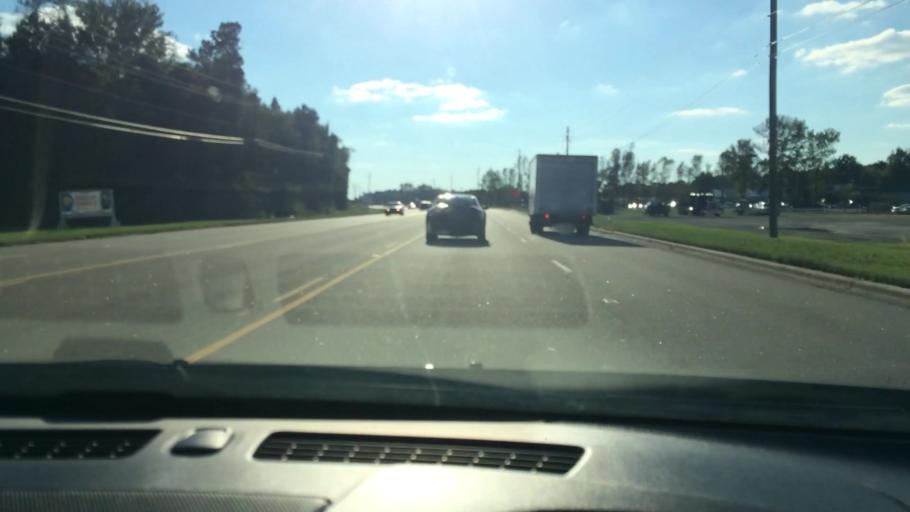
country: US
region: North Carolina
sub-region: Pitt County
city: Summerfield
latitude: 35.5743
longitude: -77.4388
